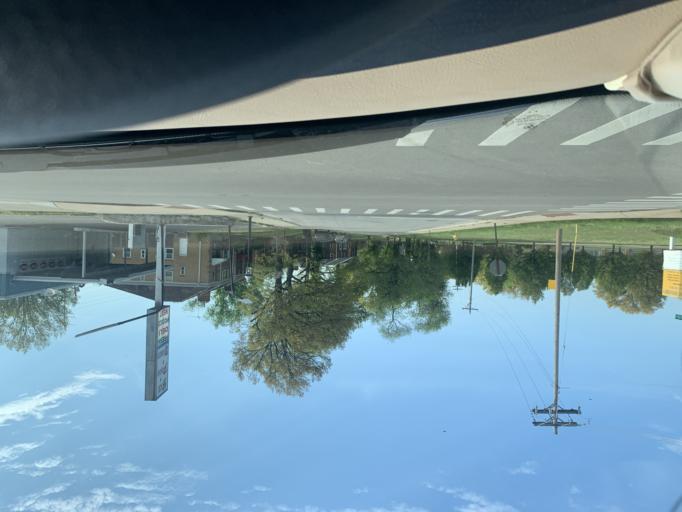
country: US
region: Ohio
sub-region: Hamilton County
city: Golf Manor
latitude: 39.1919
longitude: -84.4559
